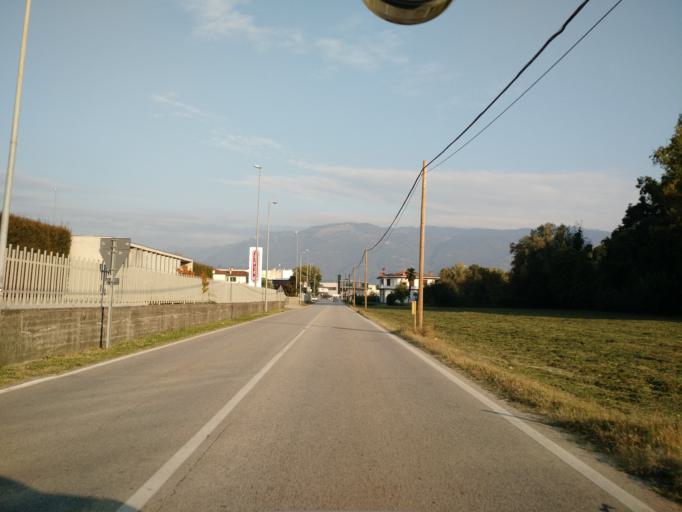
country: IT
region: Veneto
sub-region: Provincia di Vicenza
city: Breganze
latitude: 45.7079
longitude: 11.5466
